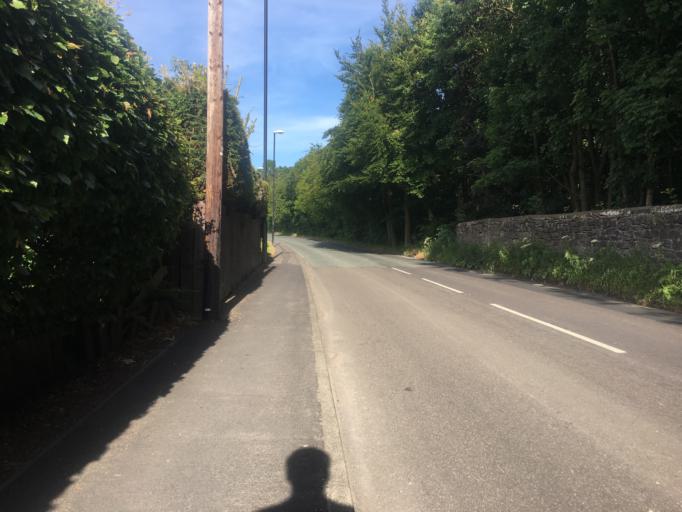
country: GB
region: England
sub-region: County Durham
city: Chester-le-Street
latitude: 54.8759
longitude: -1.5532
